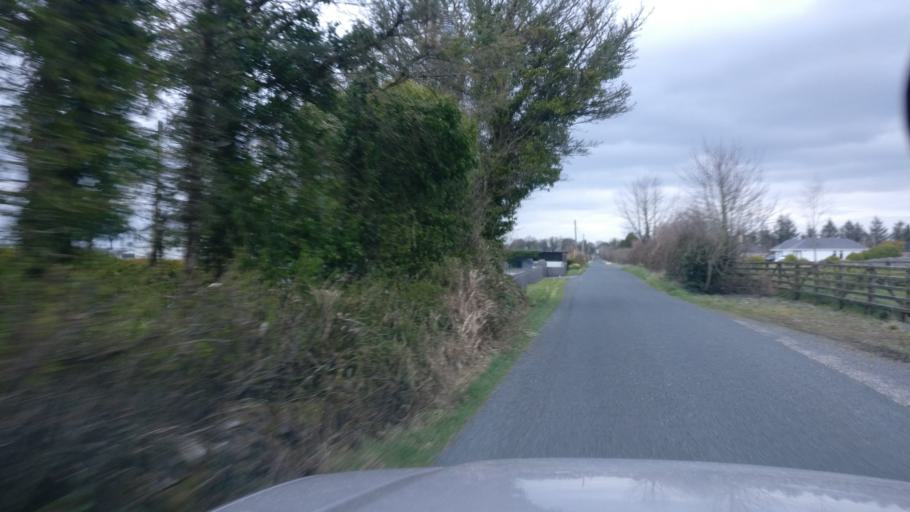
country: IE
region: Connaught
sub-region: County Galway
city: Loughrea
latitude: 53.2434
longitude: -8.5179
